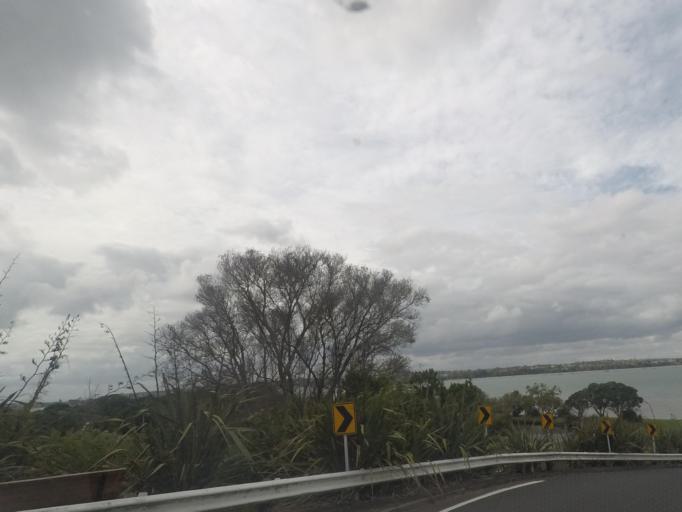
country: NZ
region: Auckland
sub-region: Auckland
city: Tamaki
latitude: -36.8719
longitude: 174.8817
